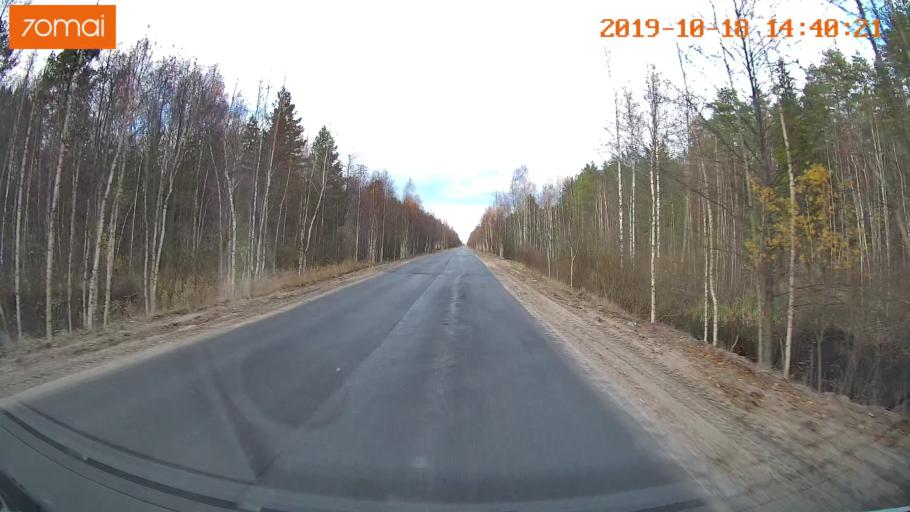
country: RU
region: Vladimir
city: Velikodvorskiy
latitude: 55.2754
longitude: 40.6688
